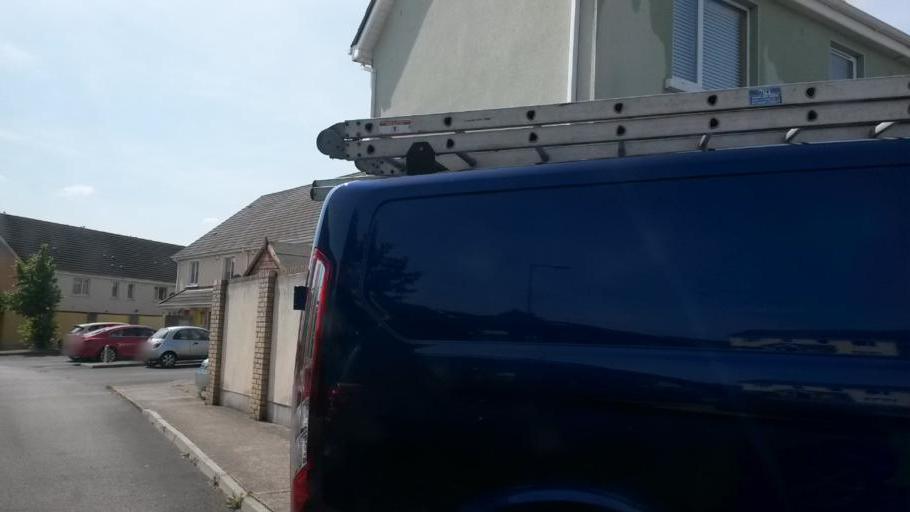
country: IE
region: Leinster
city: Lusk
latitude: 53.5227
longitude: -6.1734
